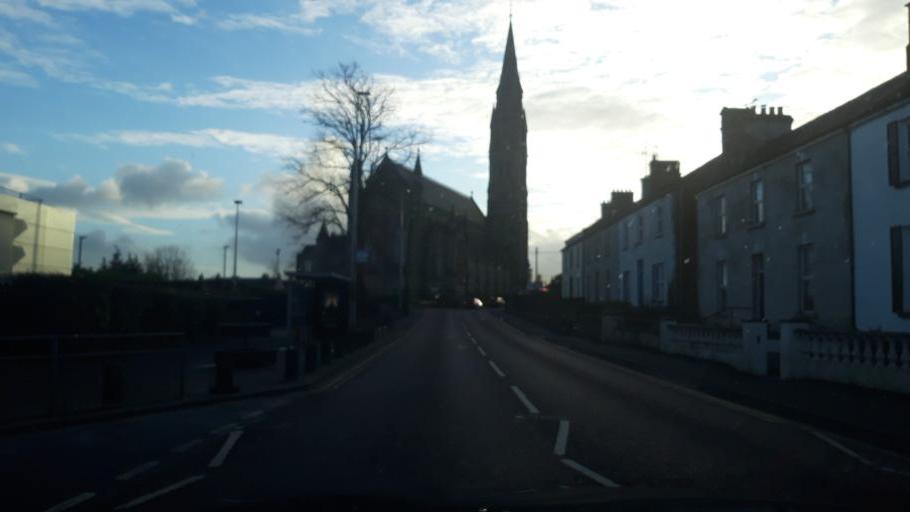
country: GB
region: Northern Ireland
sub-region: Dungannon District
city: Dungannon
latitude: 54.5066
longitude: -6.7636
